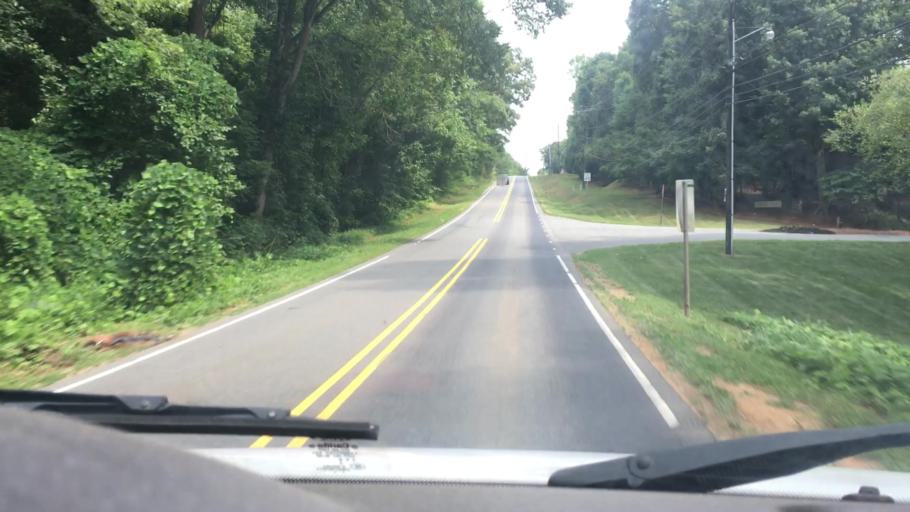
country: US
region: North Carolina
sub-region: Gaston County
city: Davidson
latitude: 35.4616
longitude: -80.8079
